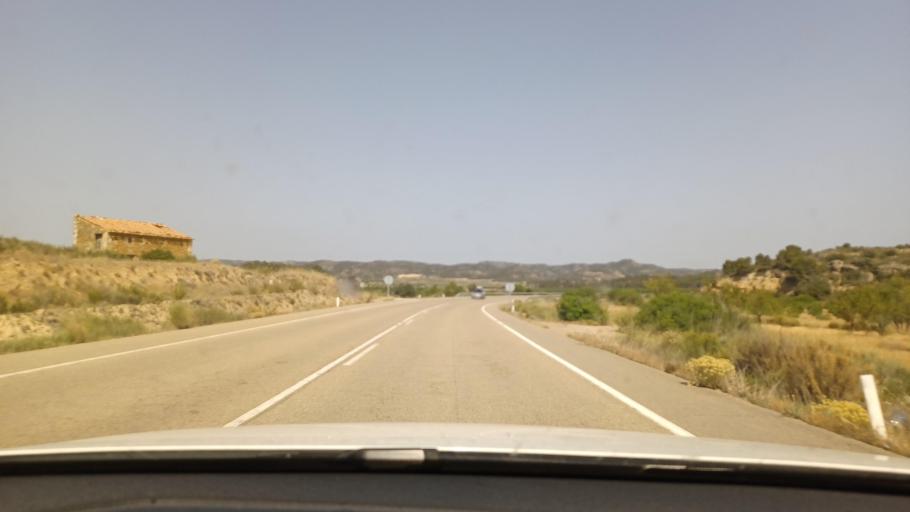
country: ES
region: Aragon
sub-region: Provincia de Zaragoza
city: Maella
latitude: 41.1053
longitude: 0.1902
